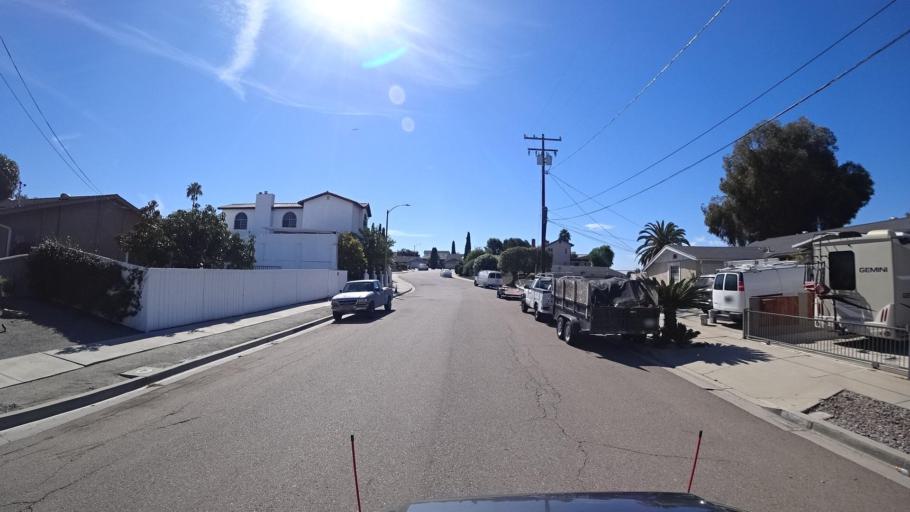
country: US
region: California
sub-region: San Diego County
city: La Presa
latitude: 32.7063
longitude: -117.0058
